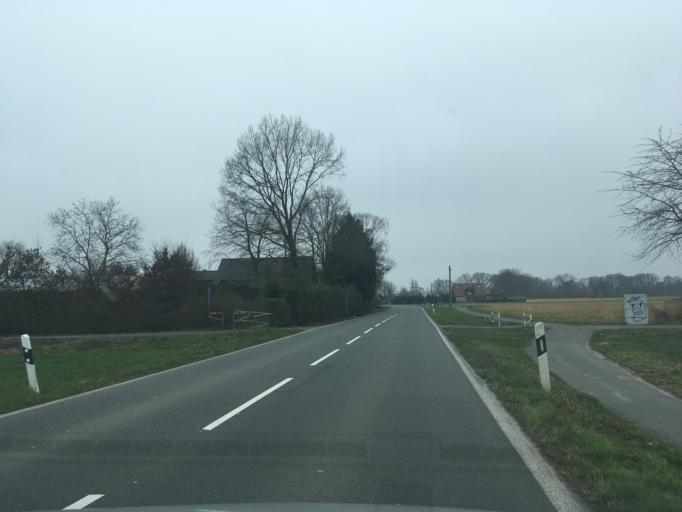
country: DE
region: North Rhine-Westphalia
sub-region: Regierungsbezirk Munster
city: Borken
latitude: 51.8393
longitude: 6.8221
